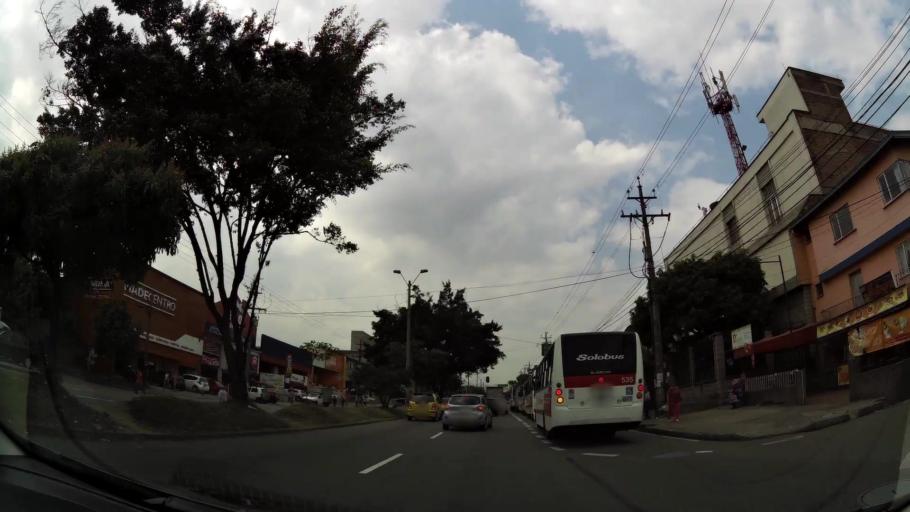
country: CO
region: Antioquia
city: Itagui
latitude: 6.2009
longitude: -75.5869
